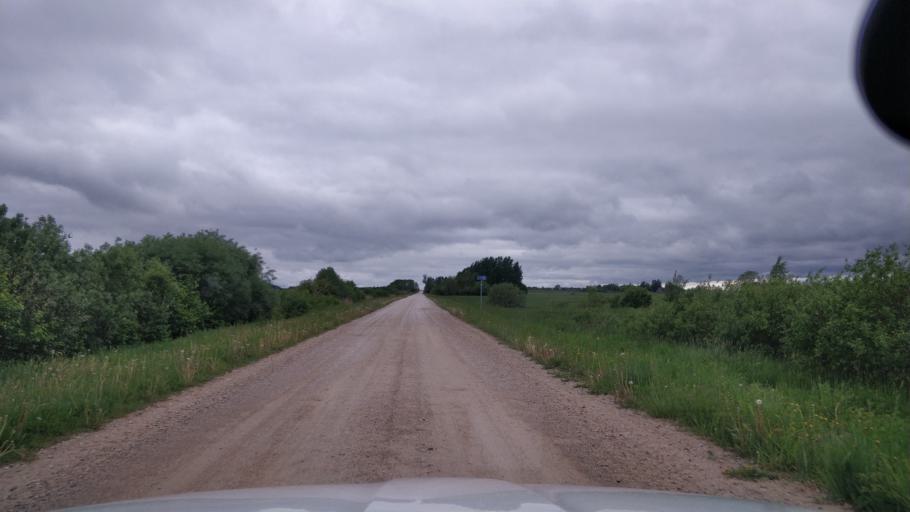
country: EE
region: Raplamaa
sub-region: Maerjamaa vald
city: Marjamaa
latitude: 58.7158
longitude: 24.2666
